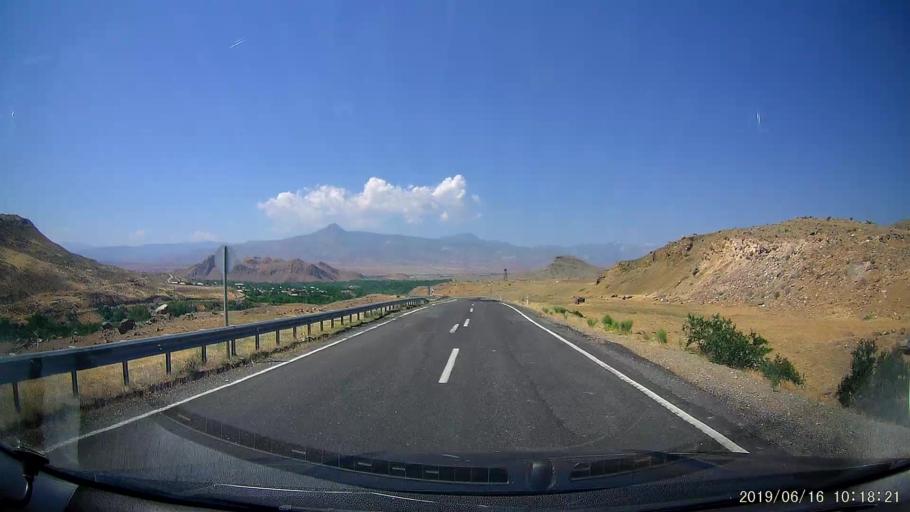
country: TR
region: Igdir
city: Tuzluca
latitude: 40.1613
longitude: 43.6692
